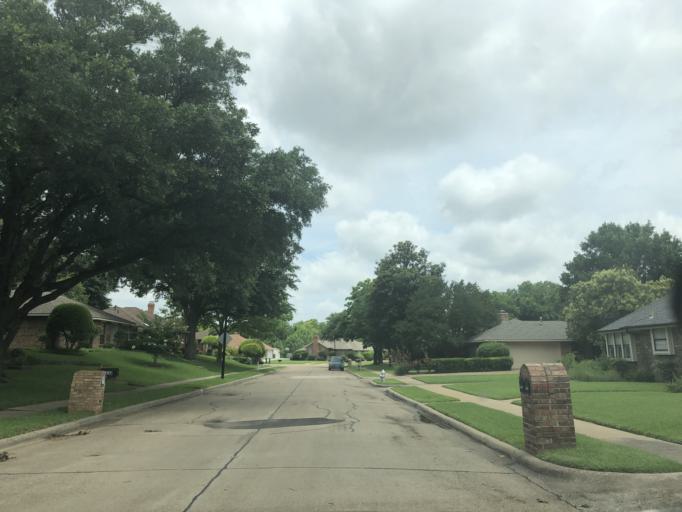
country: US
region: Texas
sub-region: Dallas County
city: Garland
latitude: 32.8518
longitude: -96.6169
